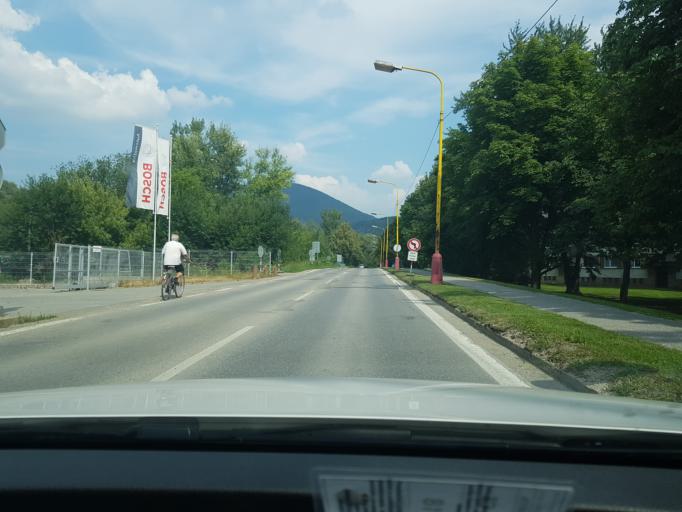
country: SK
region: Trenciansky
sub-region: Okres Povazska Bystrica
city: Povazska Bystrica
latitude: 49.1199
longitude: 18.4459
